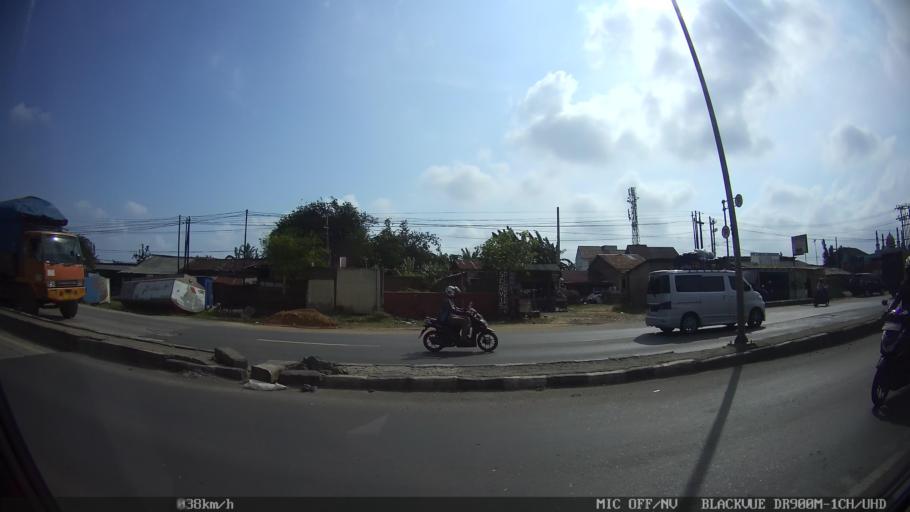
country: ID
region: Lampung
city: Kedaton
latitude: -5.3606
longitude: 105.2563
